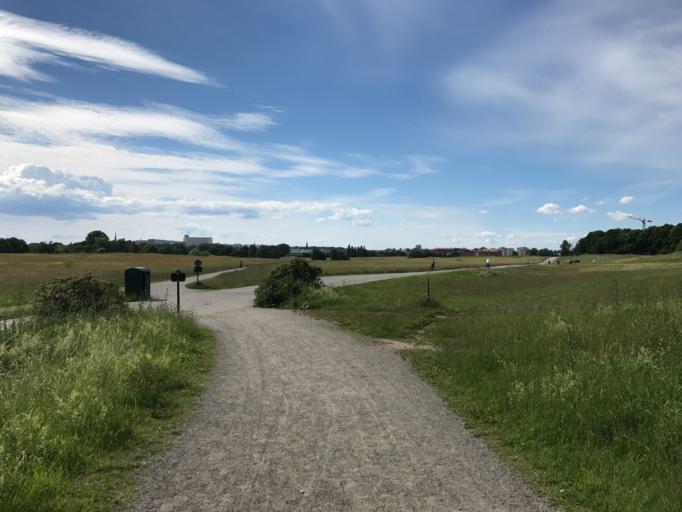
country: SE
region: Stockholm
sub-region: Lidingo
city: Lidingoe
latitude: 59.3343
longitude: 18.1230
